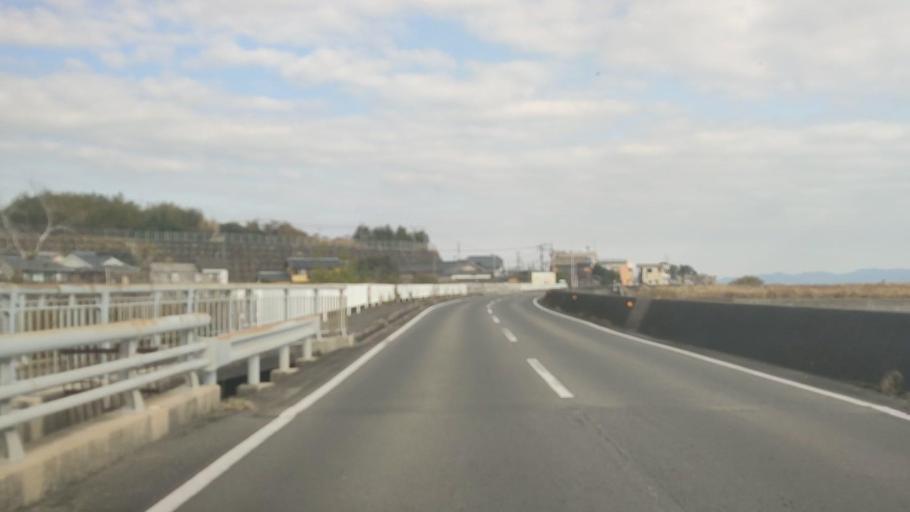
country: JP
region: Nagasaki
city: Shimabara
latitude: 32.6709
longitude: 130.3355
